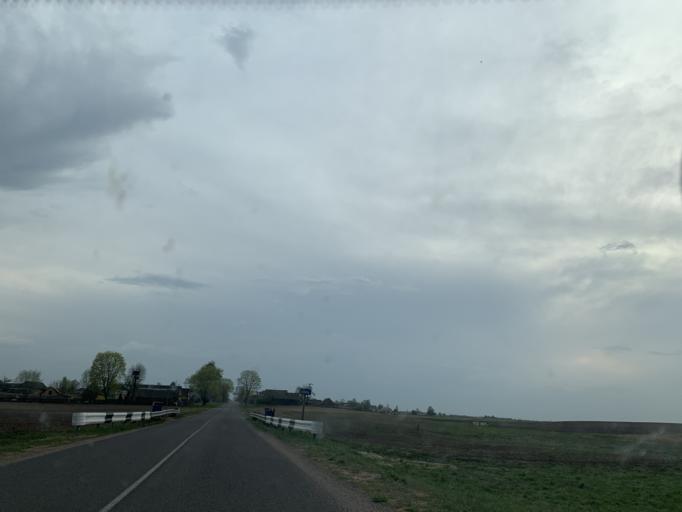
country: BY
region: Minsk
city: Kapyl'
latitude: 53.2867
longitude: 26.9863
